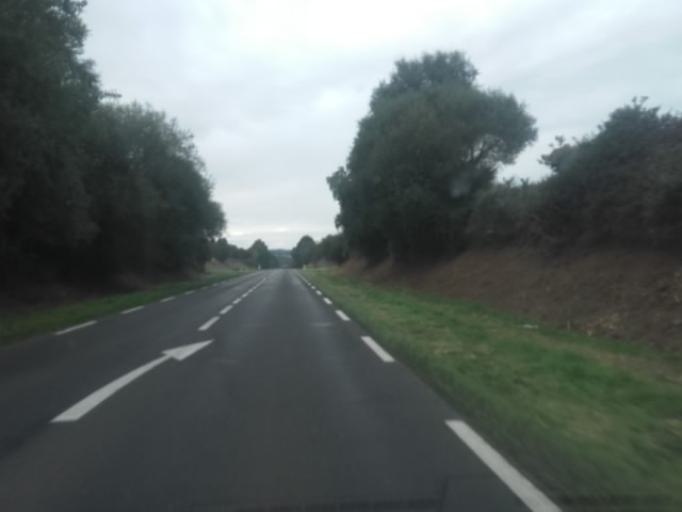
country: FR
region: Brittany
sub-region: Departement des Cotes-d'Armor
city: Lantic
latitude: 48.5627
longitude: -2.8927
